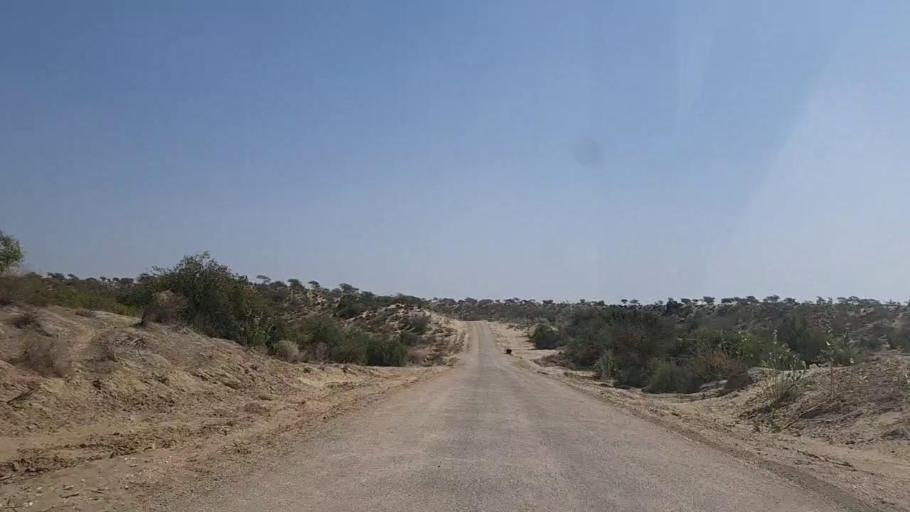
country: PK
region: Sindh
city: Diplo
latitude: 24.4795
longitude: 69.4995
